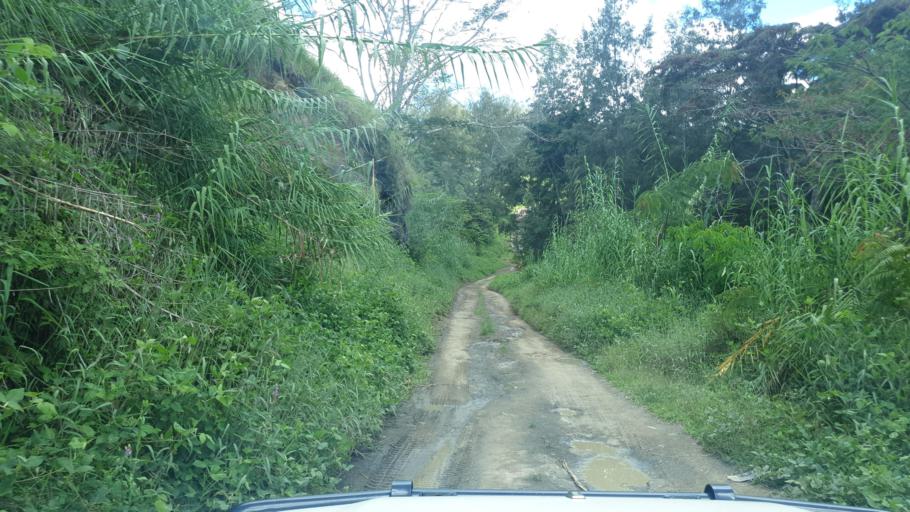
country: PG
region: Chimbu
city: Kundiawa
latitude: -6.2575
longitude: 145.1379
